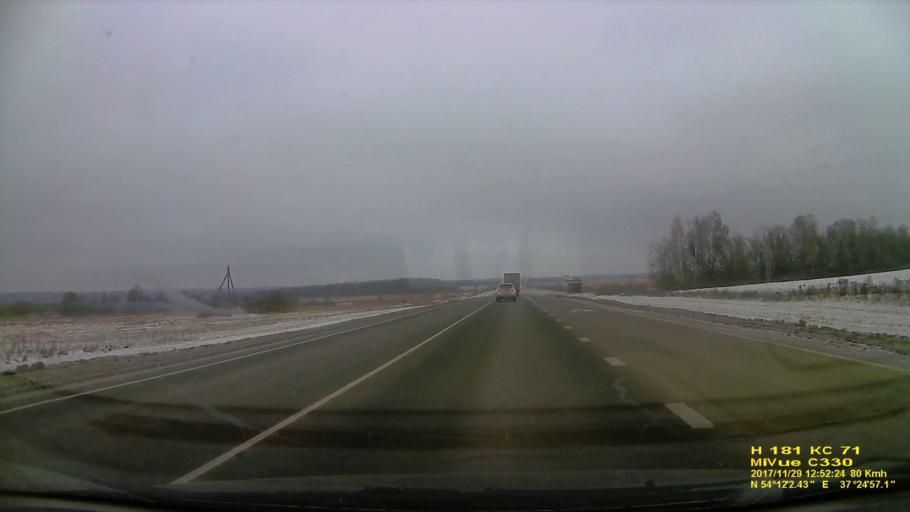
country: RU
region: Tula
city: Barsuki
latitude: 54.2006
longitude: 37.4159
